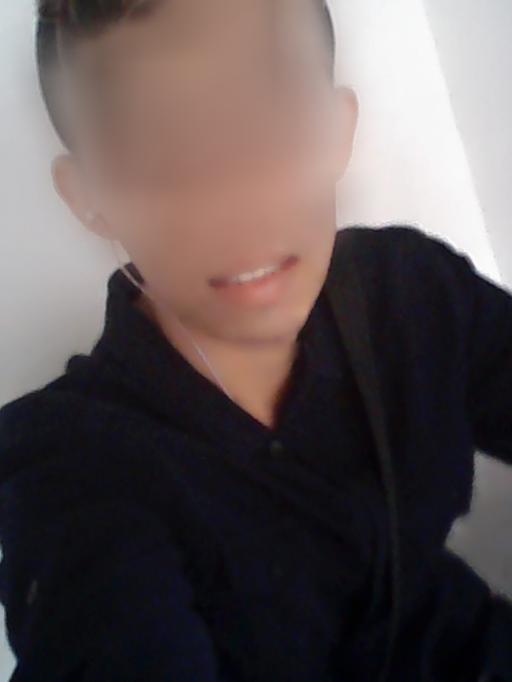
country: CO
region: Meta
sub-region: Villavicencio
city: Villavicencio
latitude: 4.1265
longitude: -73.6086
